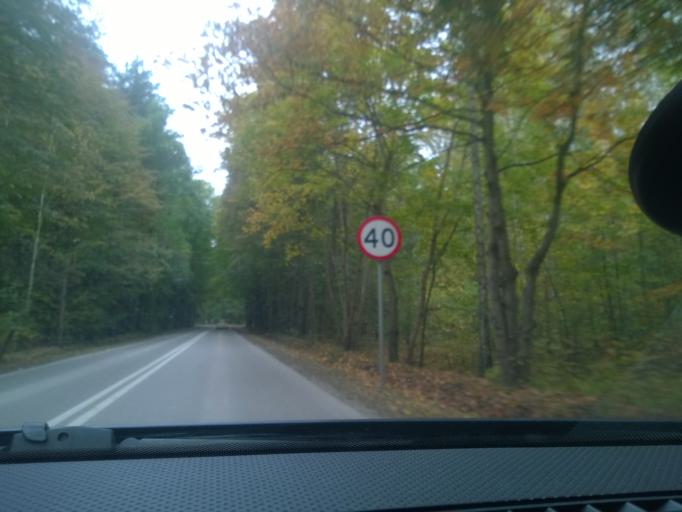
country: PL
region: Masovian Voivodeship
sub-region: Powiat pruszkowski
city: Granica
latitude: 52.1312
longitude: 20.8015
